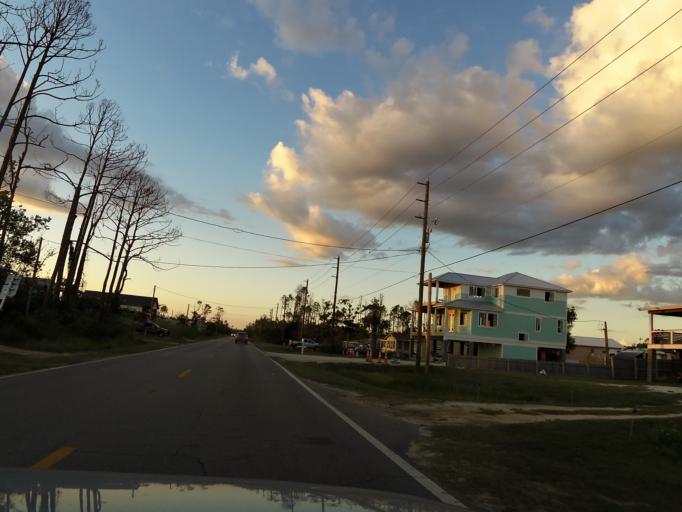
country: US
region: Florida
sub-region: Bay County
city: Mexico Beach
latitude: 29.9270
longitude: -85.3884
